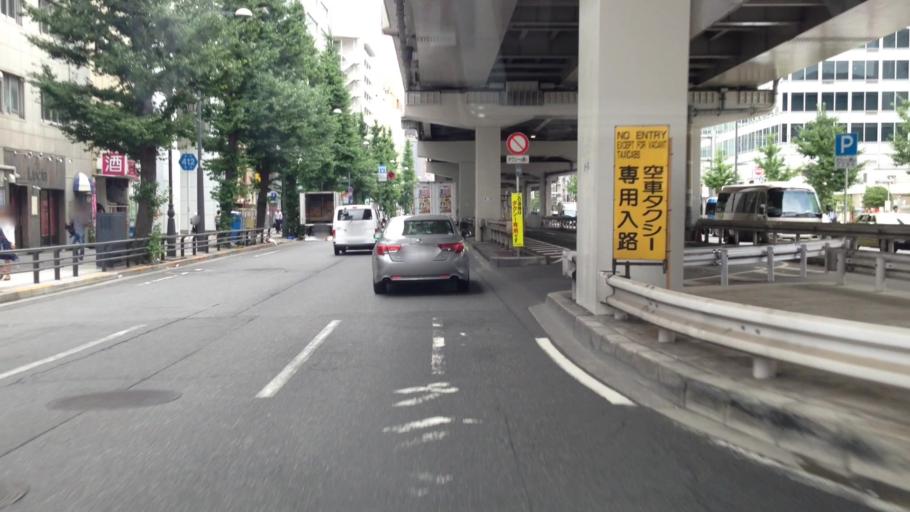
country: JP
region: Tokyo
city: Tokyo
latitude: 35.6616
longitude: 139.7286
